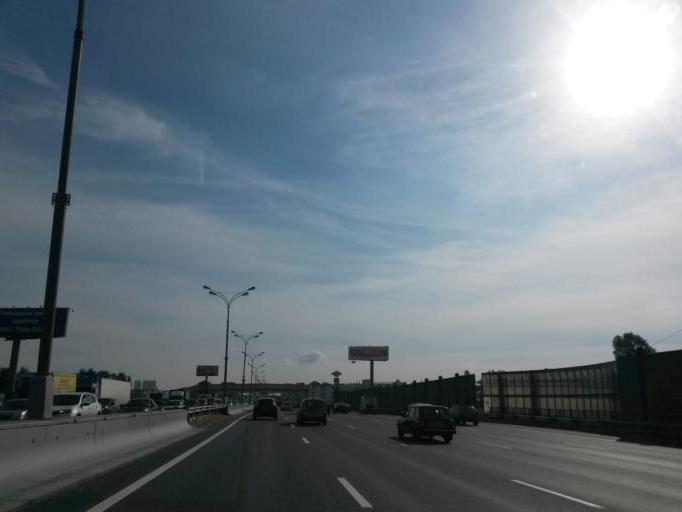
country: RU
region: Moscow
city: Biryulevo
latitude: 55.5785
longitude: 37.6952
